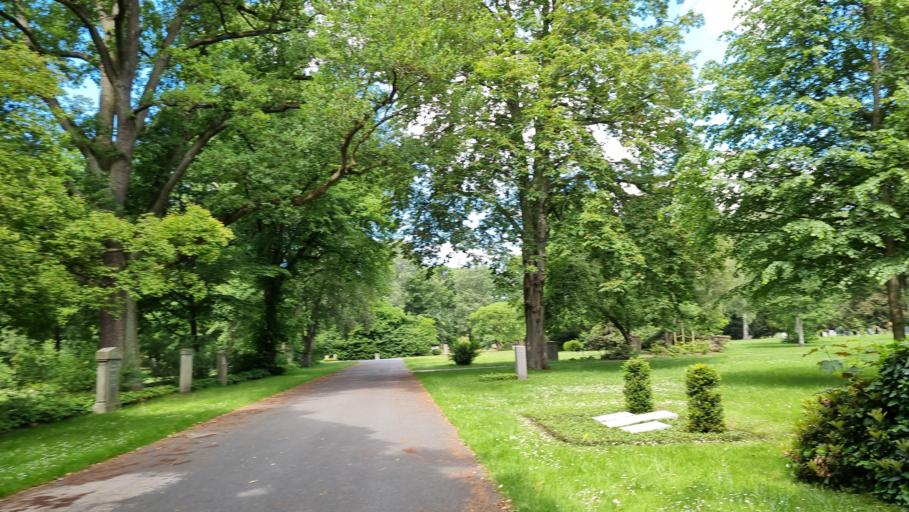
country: DE
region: Lower Saxony
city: Auf der Horst
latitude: 52.4060
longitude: 9.6710
